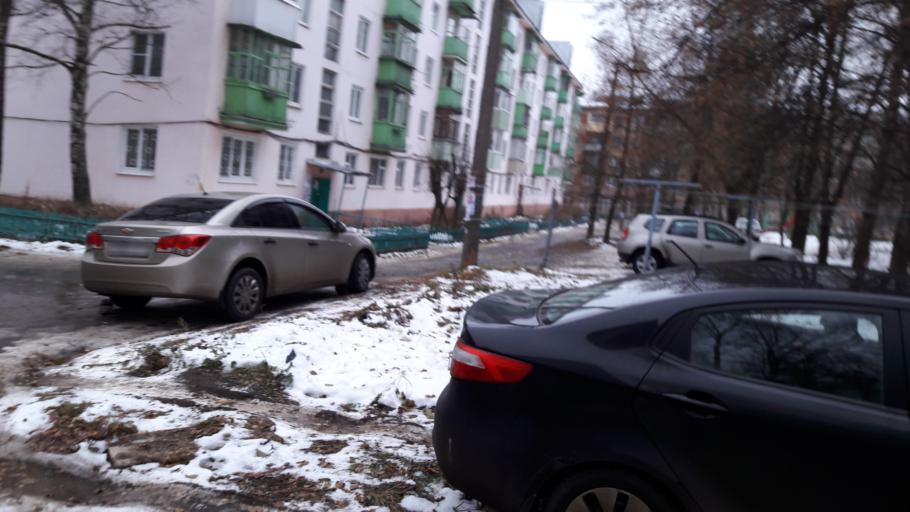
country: RU
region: Tula
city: Tula
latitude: 54.1941
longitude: 37.6870
